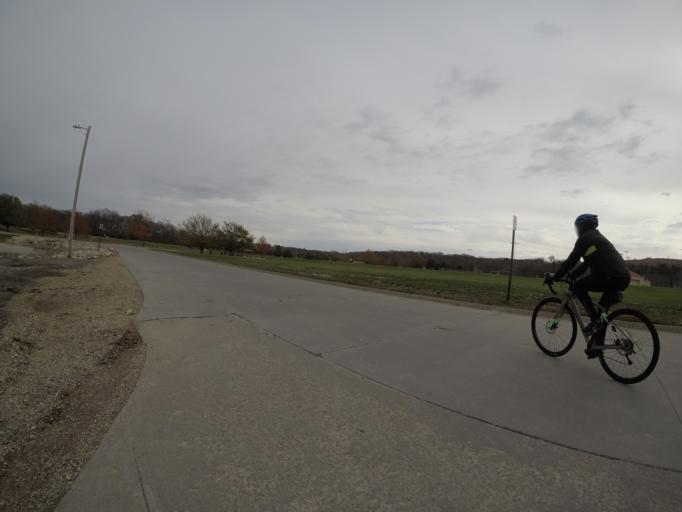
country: US
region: Kansas
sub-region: Riley County
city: Manhattan
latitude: 39.1853
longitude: -96.6323
